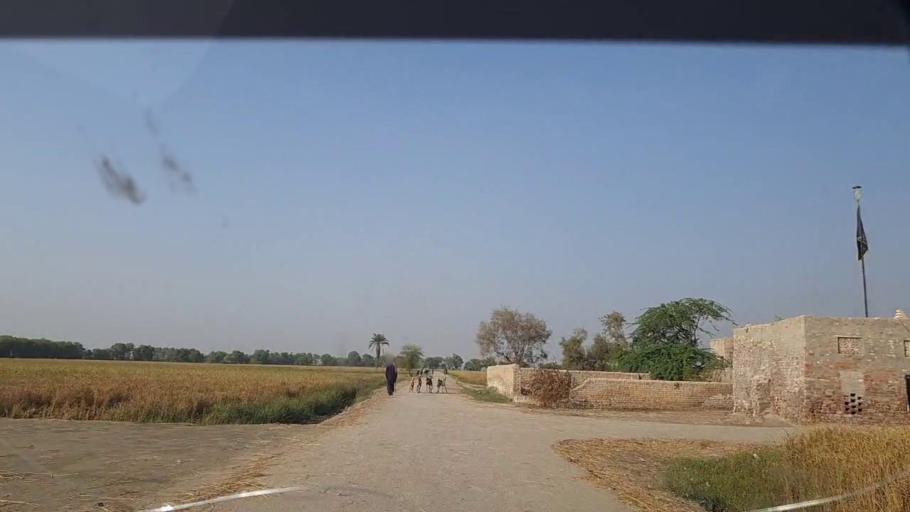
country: PK
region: Sindh
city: Shikarpur
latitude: 28.1186
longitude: 68.5834
